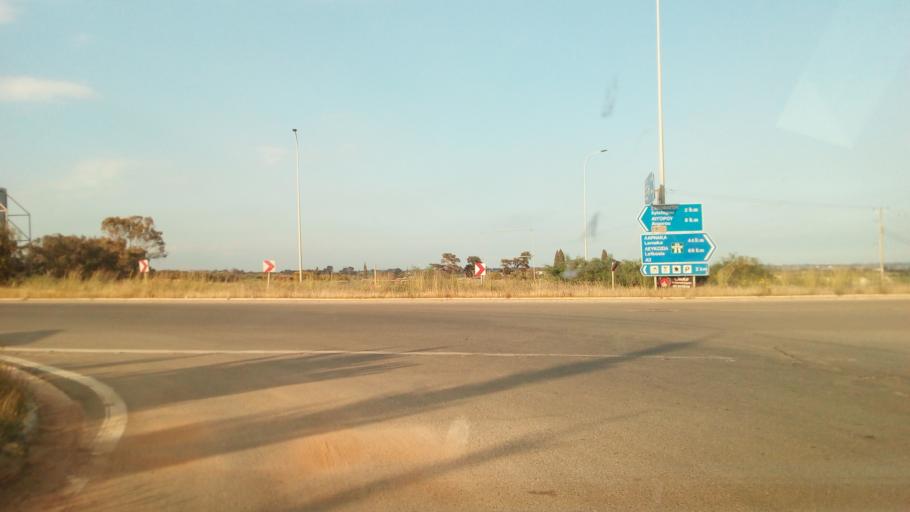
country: CY
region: Ammochostos
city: Liopetri
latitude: 34.9757
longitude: 33.8747
